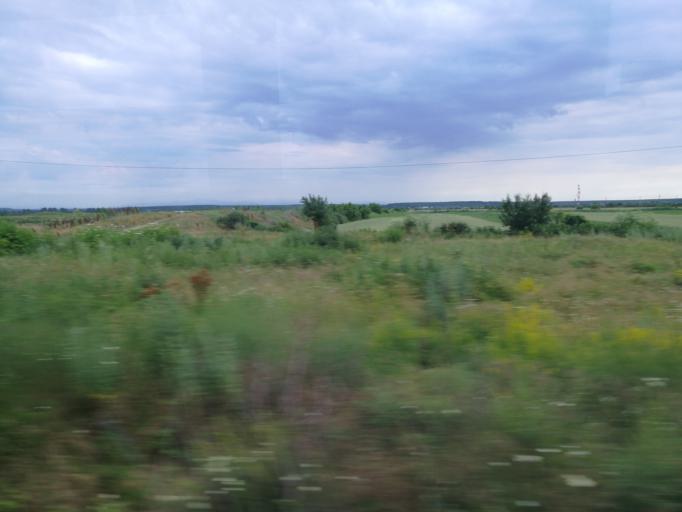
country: RO
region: Dambovita
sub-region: Comuna Petresti
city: Ionesti
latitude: 44.7188
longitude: 25.2814
